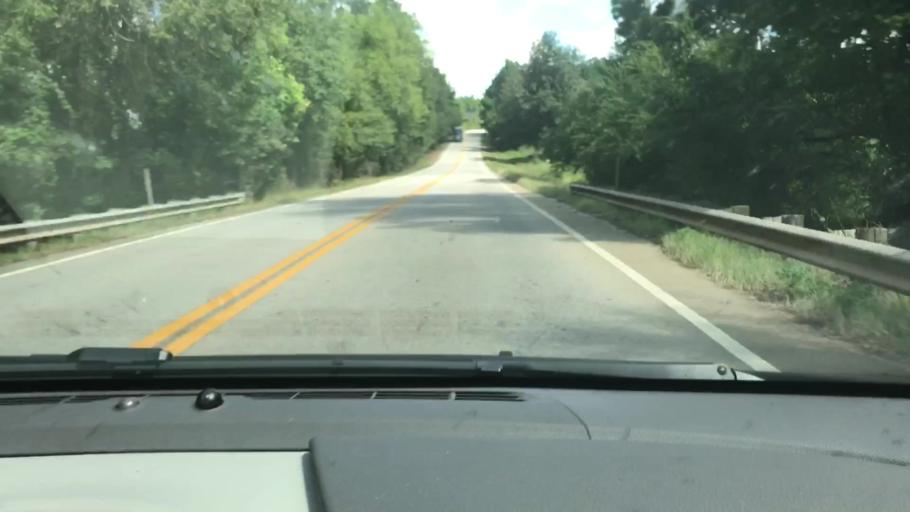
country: US
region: Georgia
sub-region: Troup County
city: La Grange
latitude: 32.9269
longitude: -85.0201
